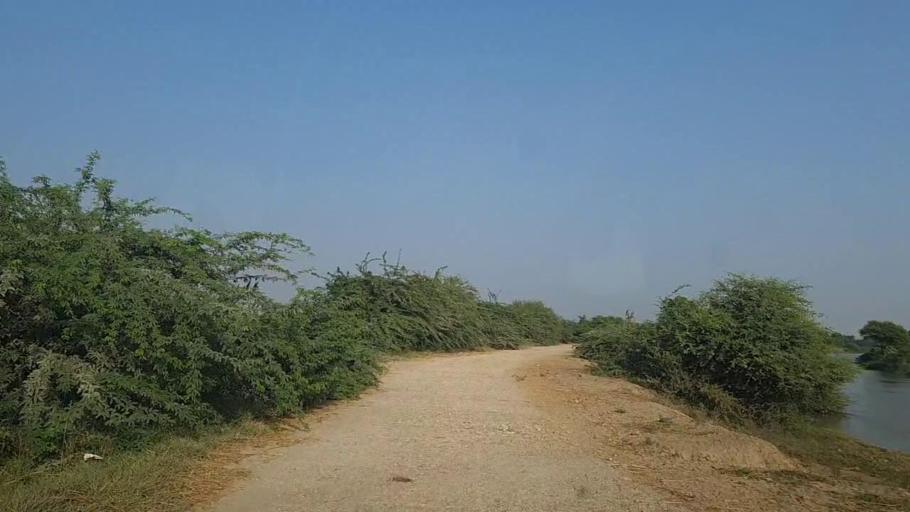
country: PK
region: Sindh
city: Mirpur Sakro
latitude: 24.5755
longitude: 67.6723
